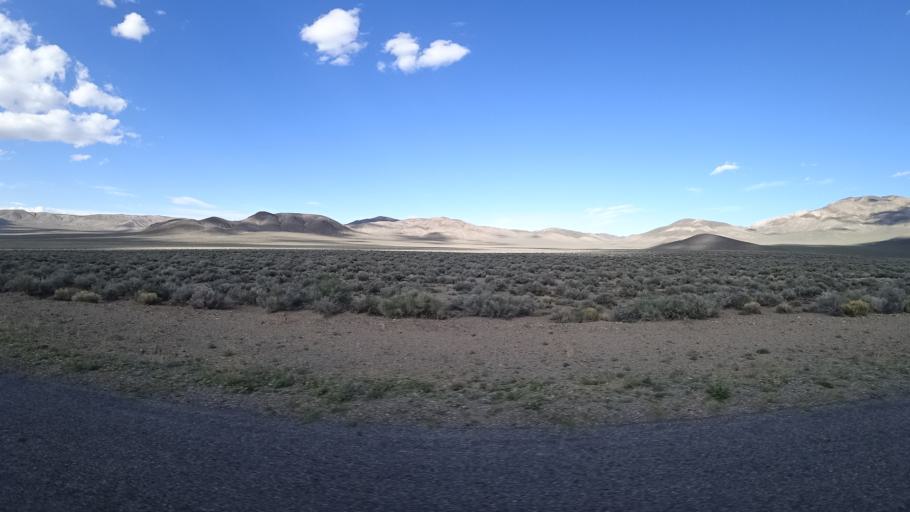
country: US
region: California
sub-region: San Bernardino County
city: Searles Valley
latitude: 36.3639
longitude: -117.1350
